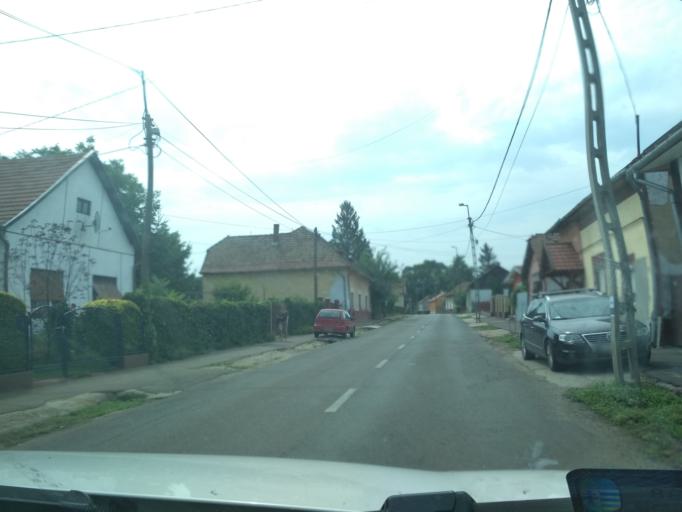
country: HU
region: Jasz-Nagykun-Szolnok
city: Tiszafured
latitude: 47.6236
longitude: 20.7544
